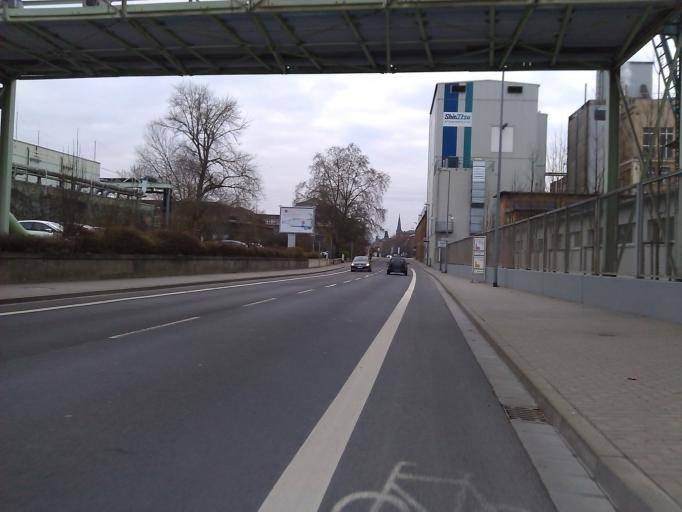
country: DE
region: Hesse
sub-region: Regierungsbezirk Darmstadt
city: Wiesbaden
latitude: 50.0323
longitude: 8.2497
